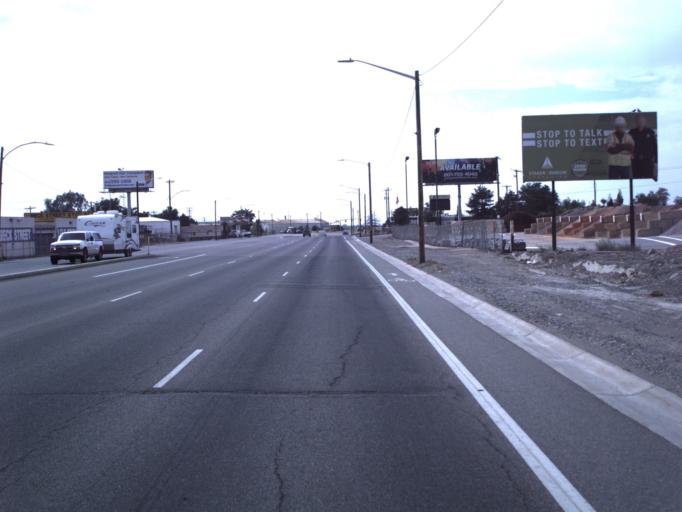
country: US
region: Utah
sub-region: Davis County
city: North Salt Lake
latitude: 40.8031
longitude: -111.9142
